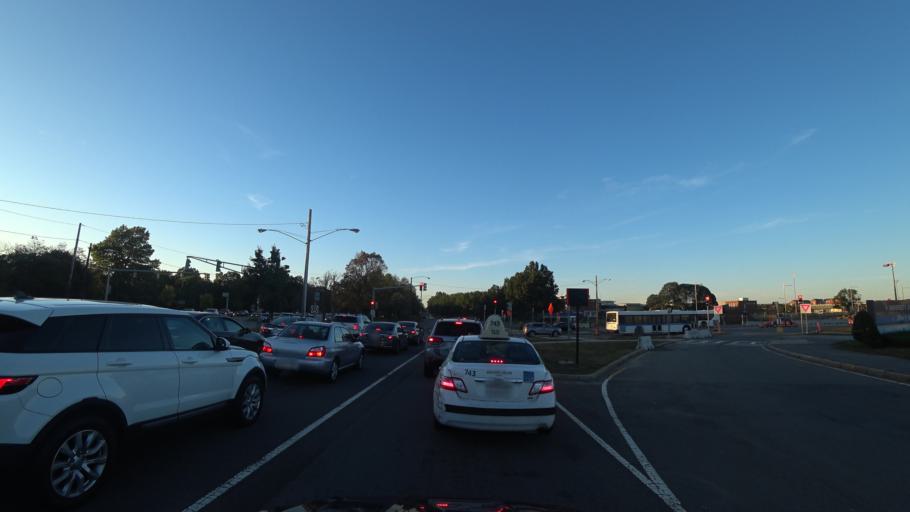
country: US
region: Massachusetts
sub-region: Suffolk County
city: South Boston
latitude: 42.3130
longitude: -71.0464
